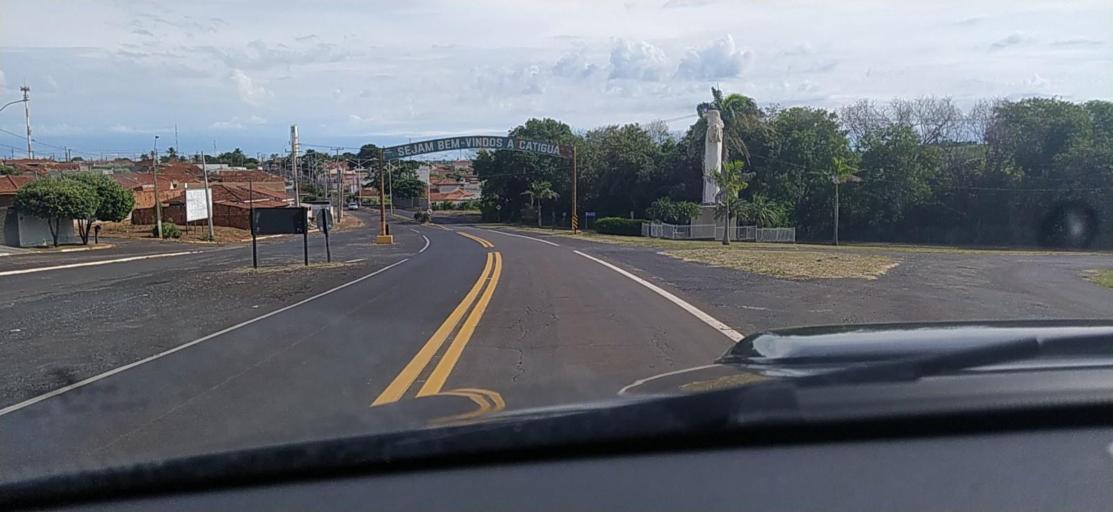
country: BR
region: Sao Paulo
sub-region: Catanduva
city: Catanduva
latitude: -21.0647
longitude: -49.0630
